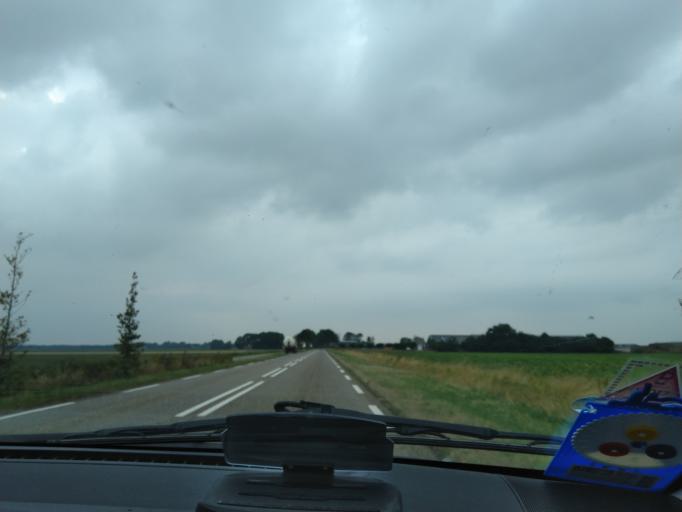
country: NL
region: Groningen
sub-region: Gemeente Vlagtwedde
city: Vlagtwedde
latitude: 53.1062
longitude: 7.1237
